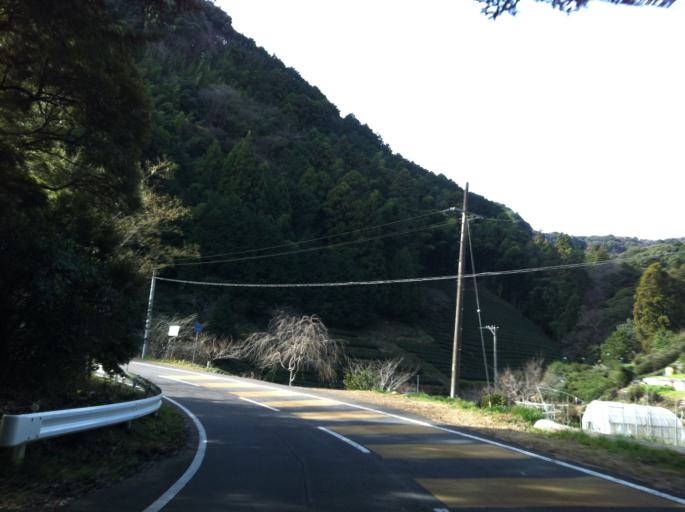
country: JP
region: Shizuoka
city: Yaizu
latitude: 34.9373
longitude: 138.3023
